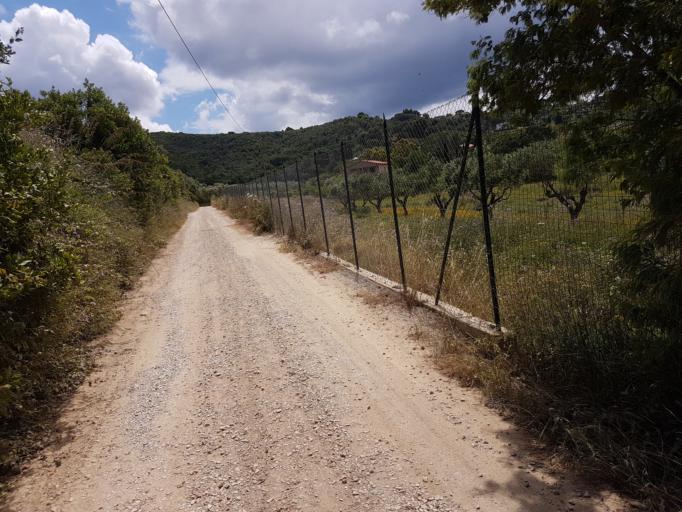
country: IT
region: Tuscany
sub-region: Provincia di Livorno
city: Portoferraio
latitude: 42.7894
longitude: 10.3521
